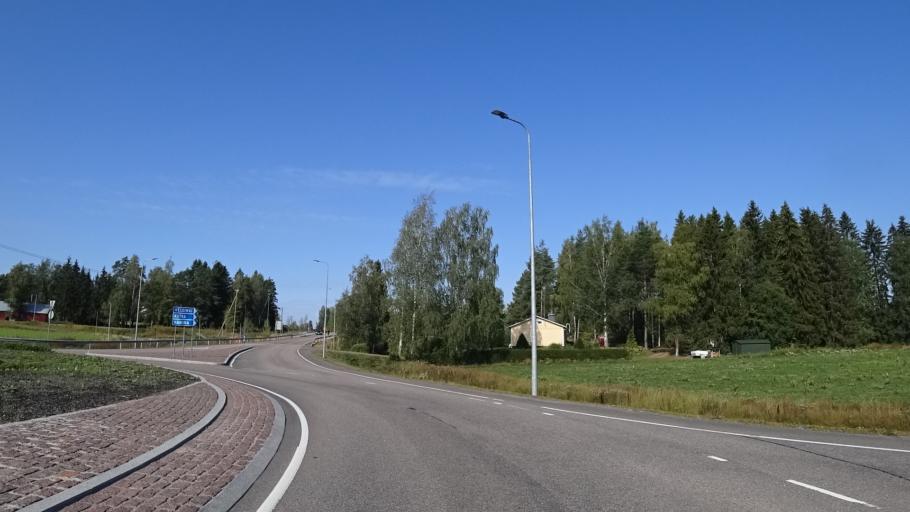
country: FI
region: Kymenlaakso
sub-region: Kotka-Hamina
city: Virojoki
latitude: 60.5880
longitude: 27.7125
